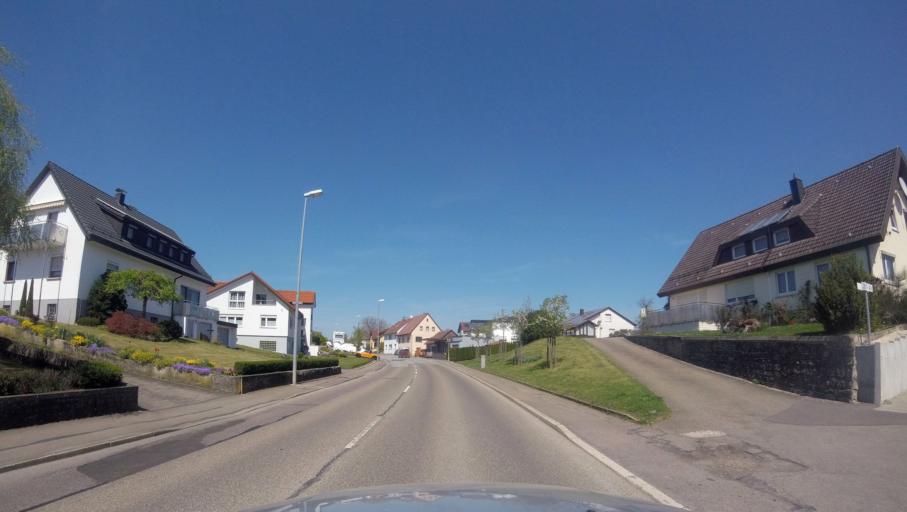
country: DE
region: Baden-Wuerttemberg
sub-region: Regierungsbezirk Stuttgart
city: Mutlangen
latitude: 48.8278
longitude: 9.7949
